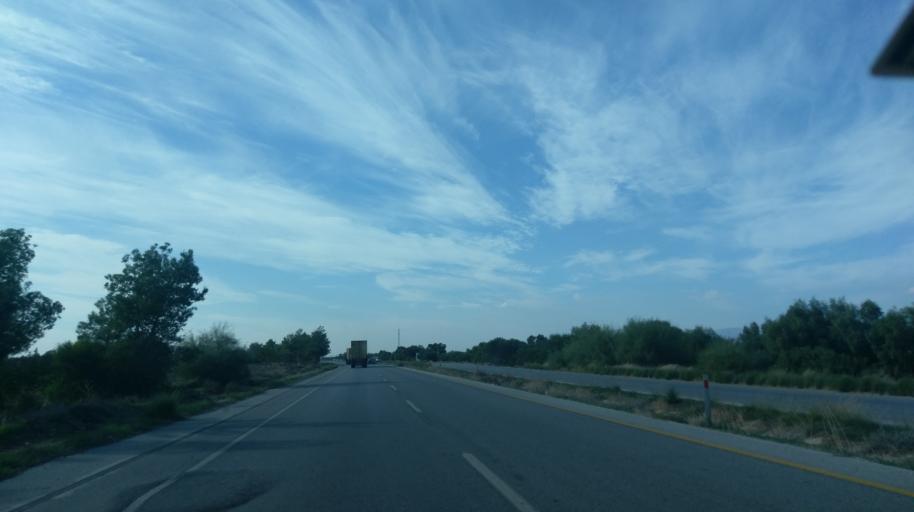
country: CY
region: Ammochostos
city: Lefkonoiko
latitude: 35.1854
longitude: 33.6623
